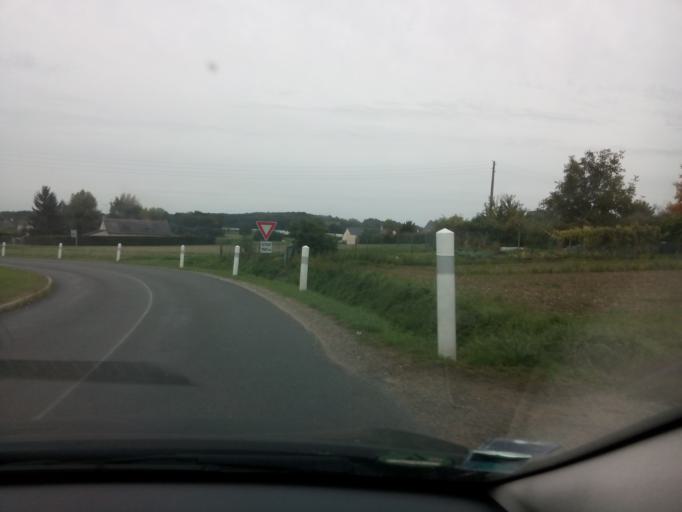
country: FR
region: Pays de la Loire
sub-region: Departement de Maine-et-Loire
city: Baune
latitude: 47.5011
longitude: -0.3231
